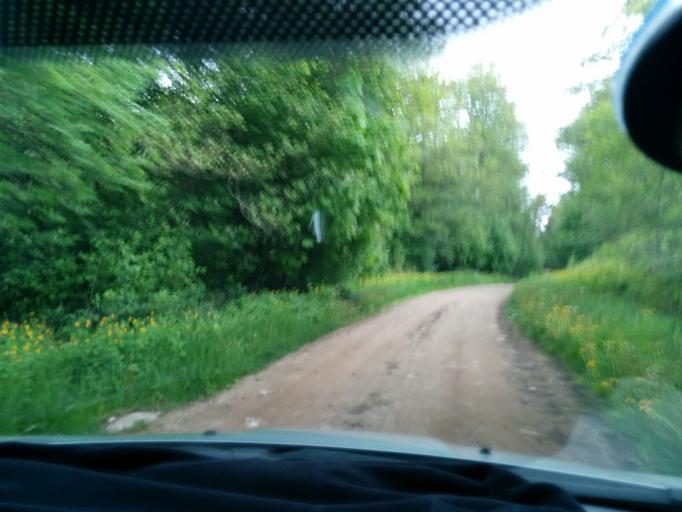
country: EE
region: Harju
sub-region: Loksa linn
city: Loksa
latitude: 59.6577
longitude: 25.6973
